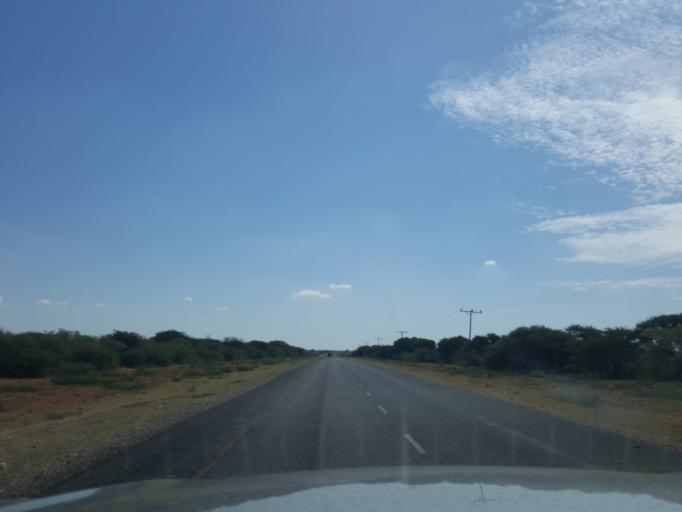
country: BW
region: Kweneng
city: Letlhakeng
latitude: -24.1197
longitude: 25.0674
